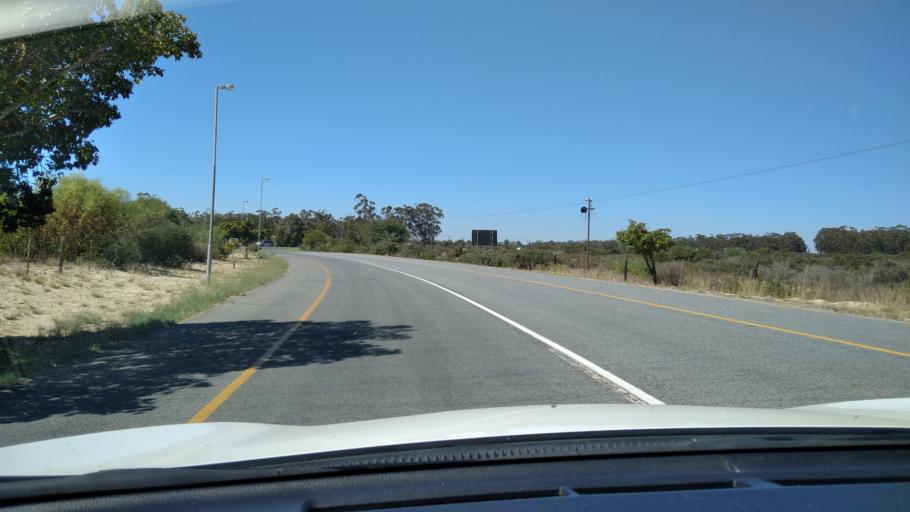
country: ZA
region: Western Cape
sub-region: West Coast District Municipality
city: Moorreesburg
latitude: -33.0637
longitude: 18.3568
